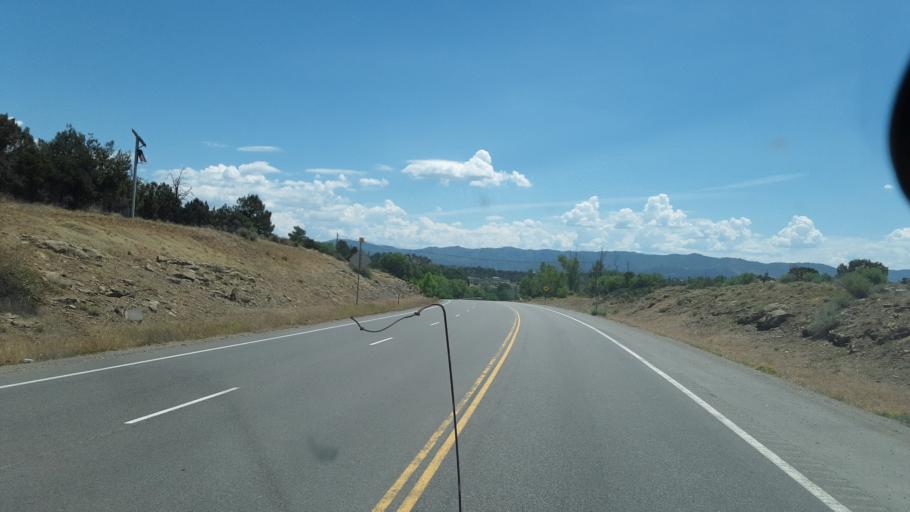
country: US
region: Colorado
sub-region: La Plata County
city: Bayfield
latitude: 37.2176
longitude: -107.6458
